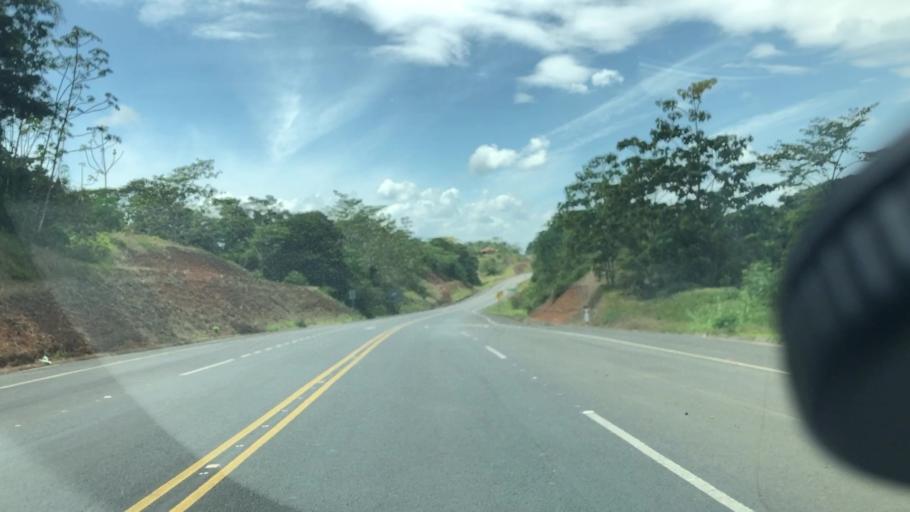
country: CR
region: Heredia
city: La Virgen
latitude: 10.4398
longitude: -84.1619
